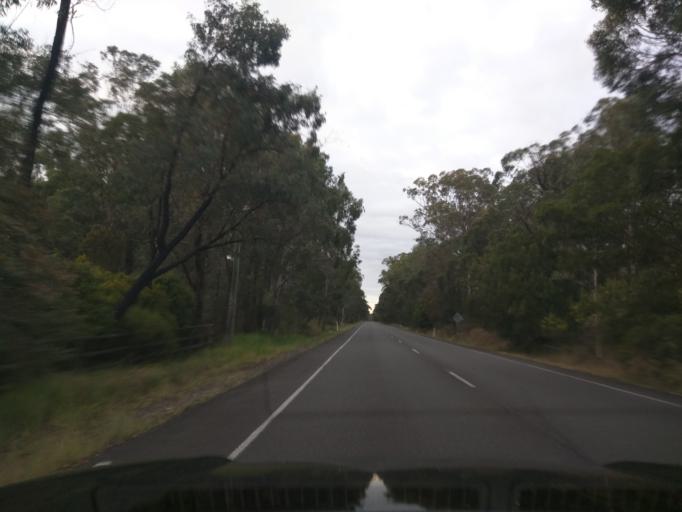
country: AU
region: New South Wales
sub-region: Wollondilly
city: Douglas Park
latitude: -34.2525
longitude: 150.7244
